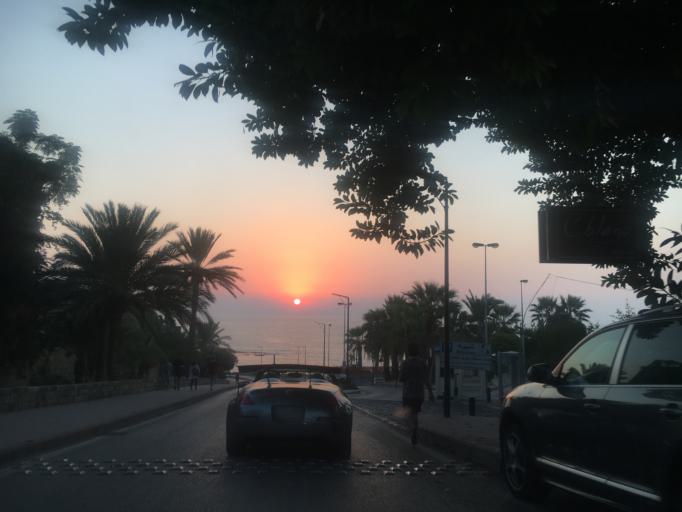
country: LB
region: Mont-Liban
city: Jbail
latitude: 34.1229
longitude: 35.6442
